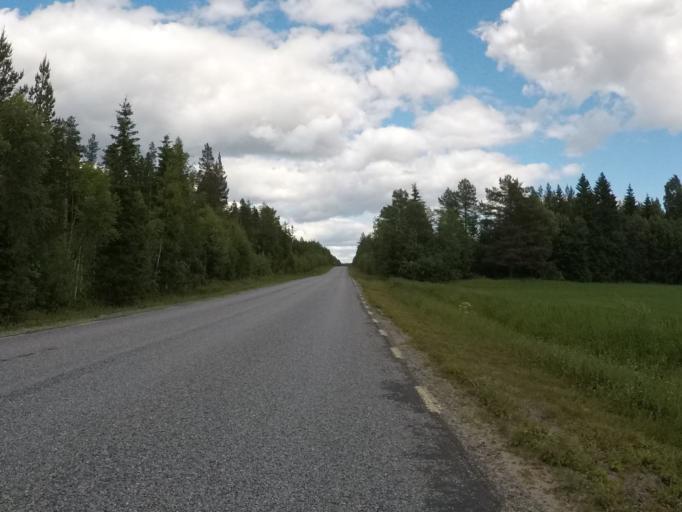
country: SE
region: Vaesterbotten
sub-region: Umea Kommun
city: Saevar
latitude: 63.9420
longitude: 20.7880
